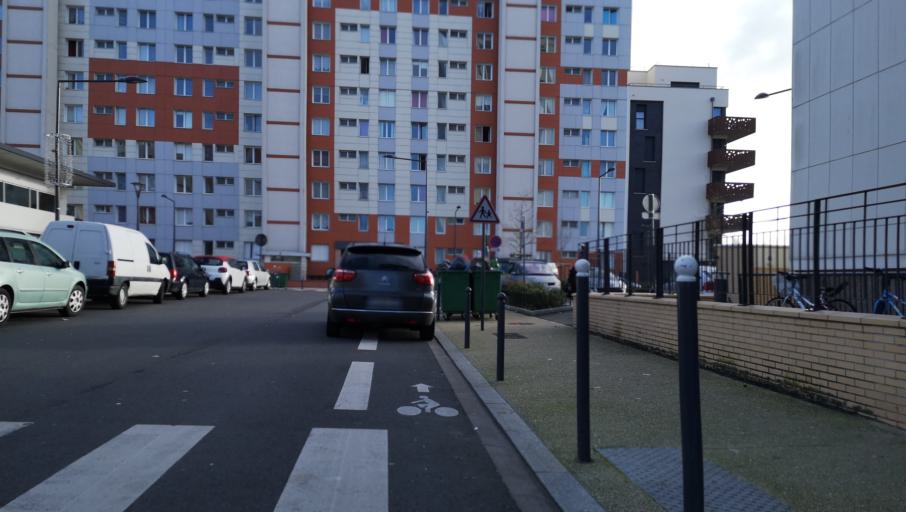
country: FR
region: Centre
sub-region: Departement du Loiret
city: Saint-Jean-le-Blanc
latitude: 47.8864
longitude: 1.9103
